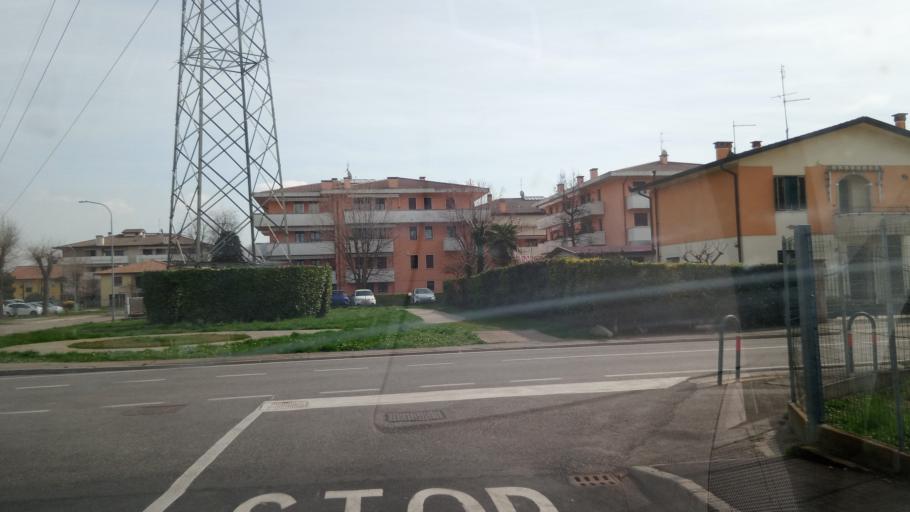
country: IT
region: Veneto
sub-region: Provincia di Padova
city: Vigodarzere
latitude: 45.4593
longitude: 11.8832
